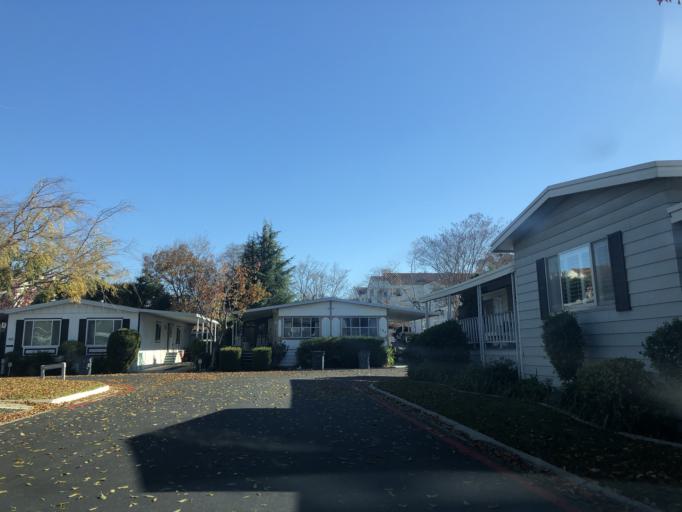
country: US
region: California
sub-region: Santa Clara County
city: Sunnyvale
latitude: 37.4002
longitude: -122.0198
